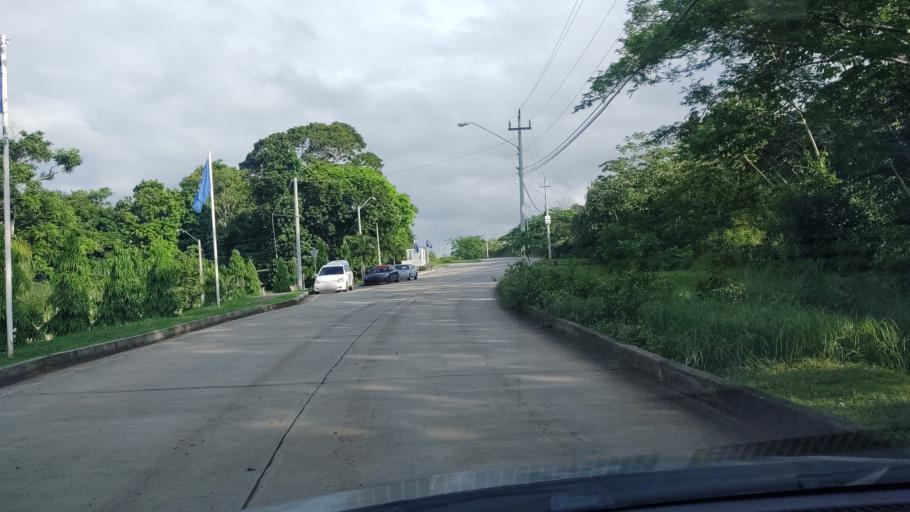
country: PA
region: Panama
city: Nuevo Arraijan
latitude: 8.9259
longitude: -79.7617
